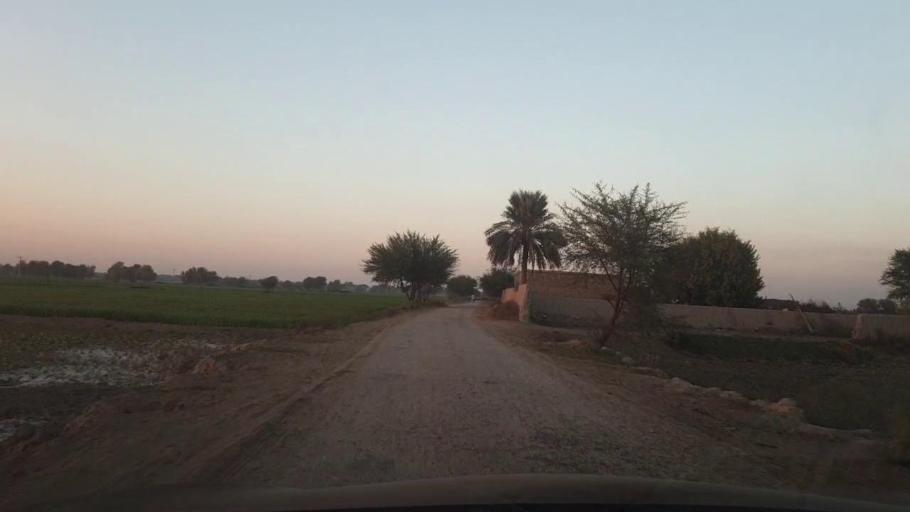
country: PK
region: Sindh
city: Ubauro
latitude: 28.1684
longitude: 69.6357
